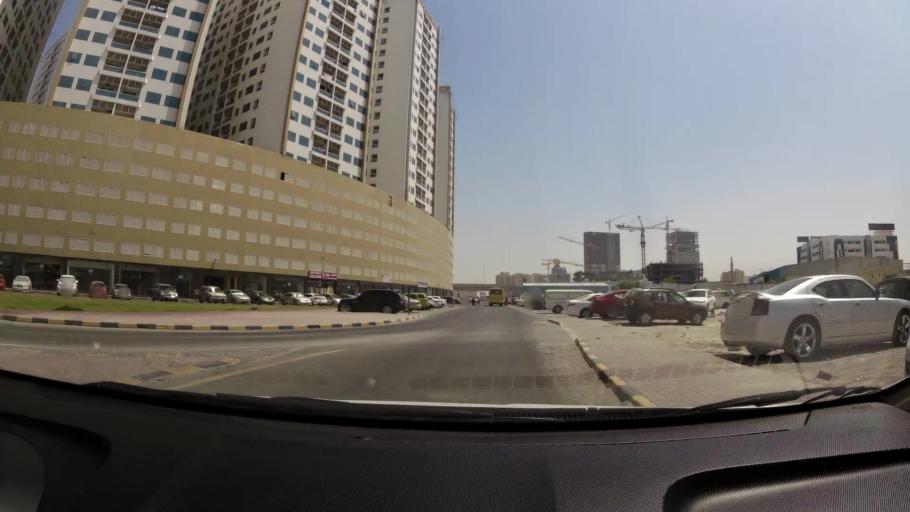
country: AE
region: Ajman
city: Ajman
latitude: 25.3916
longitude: 55.4683
